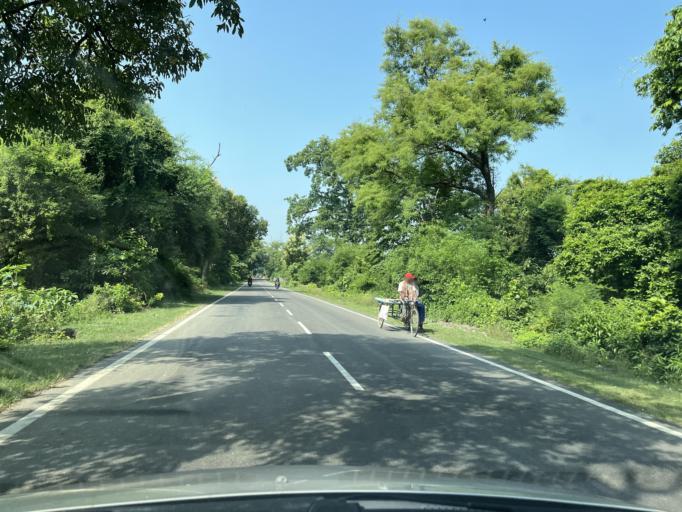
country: IN
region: Uttarakhand
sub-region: Naini Tal
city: Kaladhungi
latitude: 29.2210
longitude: 79.2354
